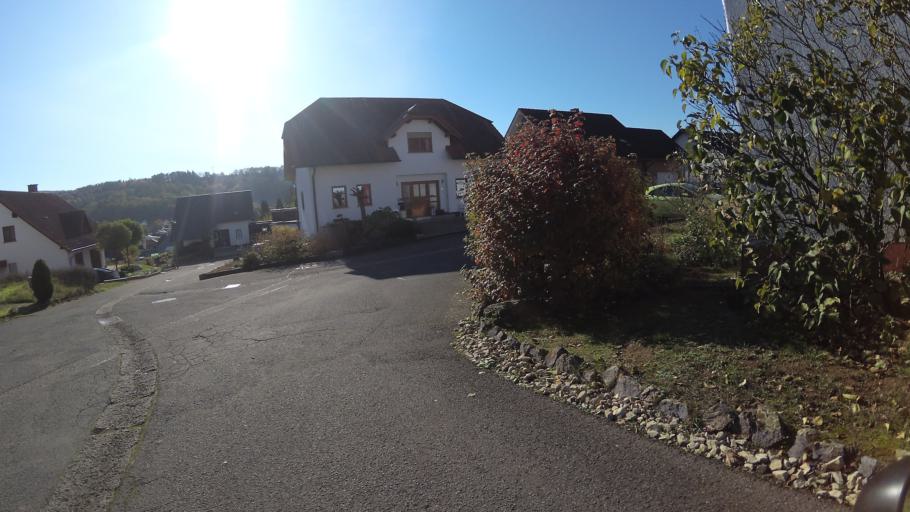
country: DE
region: Saarland
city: Britten
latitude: 49.4813
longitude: 6.7051
